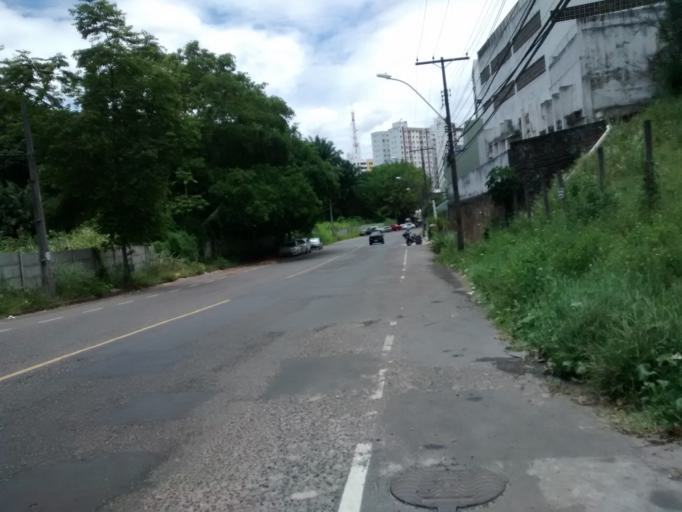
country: BR
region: Bahia
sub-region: Salvador
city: Salvador
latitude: -12.9747
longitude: -38.4413
